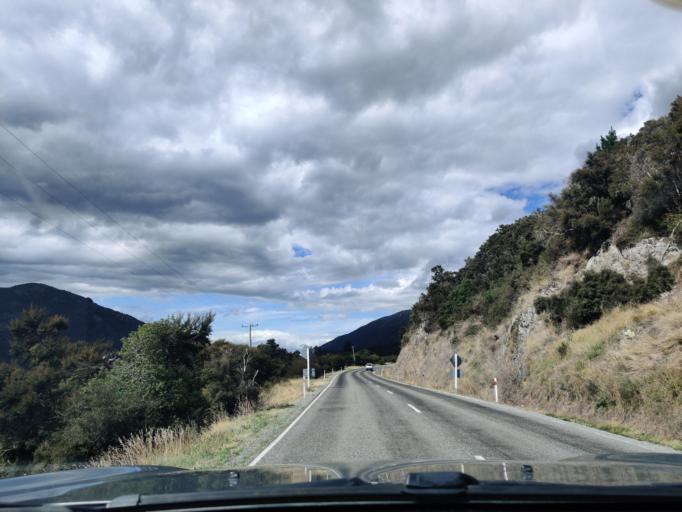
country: NZ
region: Canterbury
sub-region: Hurunui District
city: Amberley
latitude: -42.5918
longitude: 172.5754
